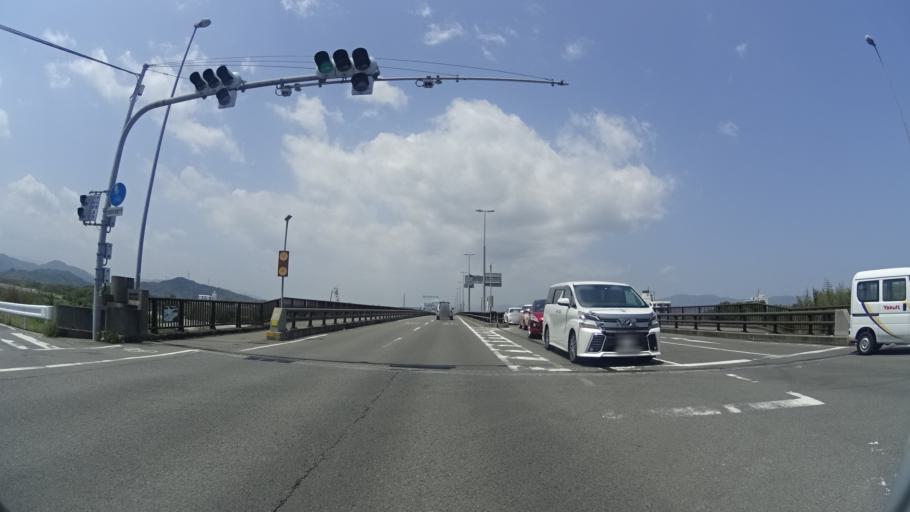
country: JP
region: Tokushima
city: Ishii
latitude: 34.0725
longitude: 134.5000
